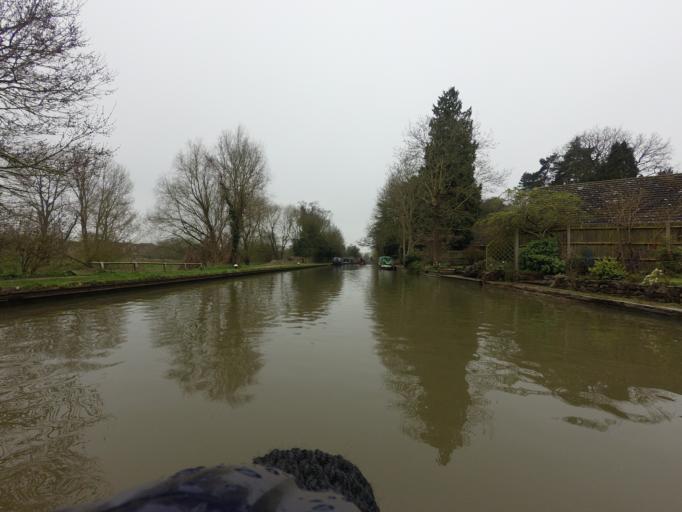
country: GB
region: England
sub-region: Central Bedfordshire
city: Leighton Buzzard
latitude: 51.9262
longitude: -0.6653
